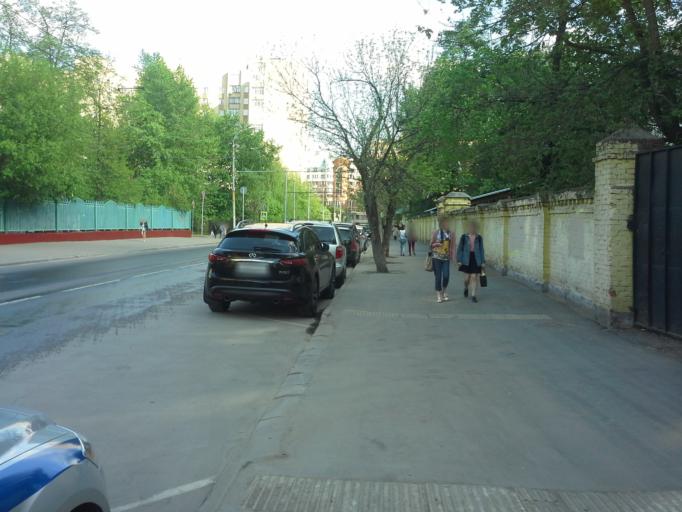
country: RU
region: Moscow
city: Mar'ina Roshcha
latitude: 55.7800
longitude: 37.5947
